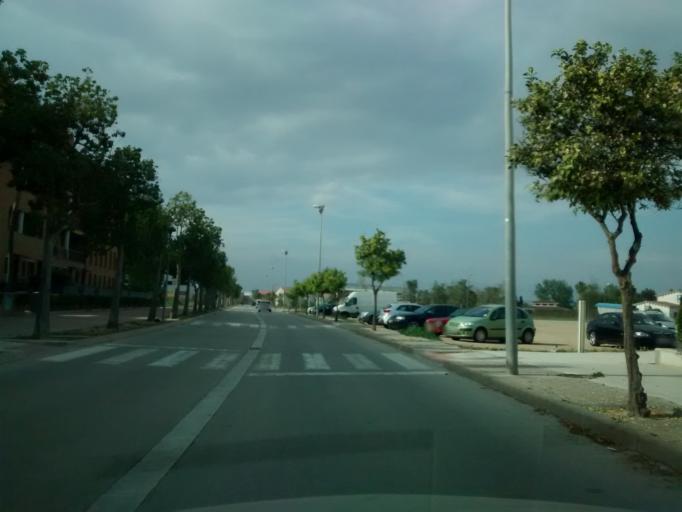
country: ES
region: Catalonia
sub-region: Provincia de Tarragona
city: Deltebre
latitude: 40.7213
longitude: 0.7212
